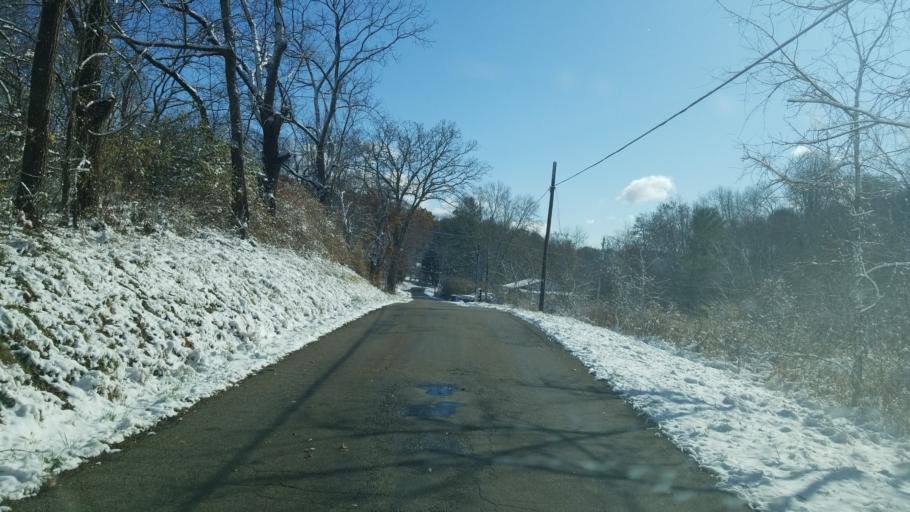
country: US
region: Ohio
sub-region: Licking County
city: Newark
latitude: 40.1525
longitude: -82.3640
